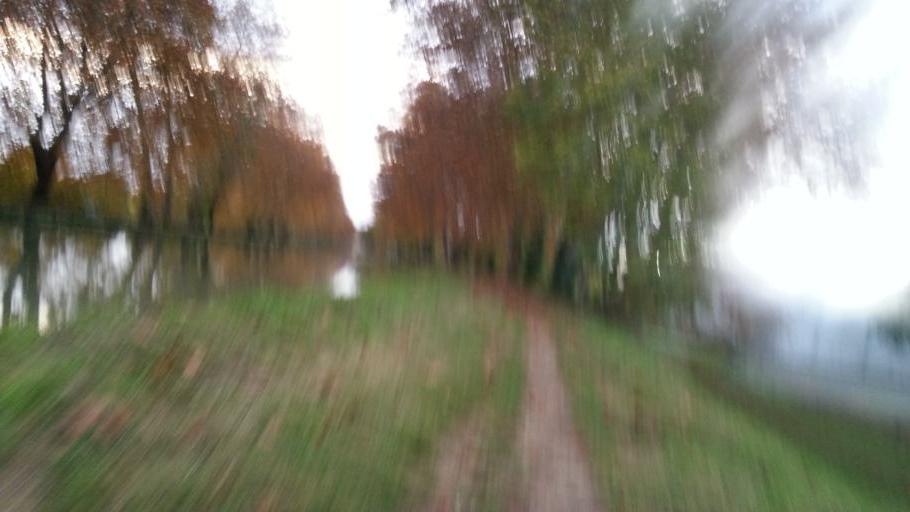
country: FR
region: Midi-Pyrenees
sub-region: Departement du Tarn-et-Garonne
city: Moissac
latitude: 44.0970
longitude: 1.1025
